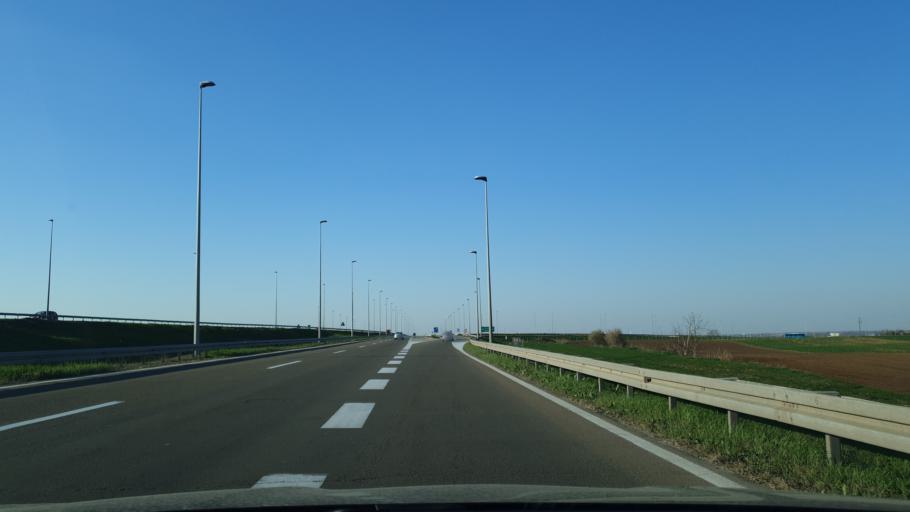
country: RS
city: Dobanovci
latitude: 44.8309
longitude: 20.2515
